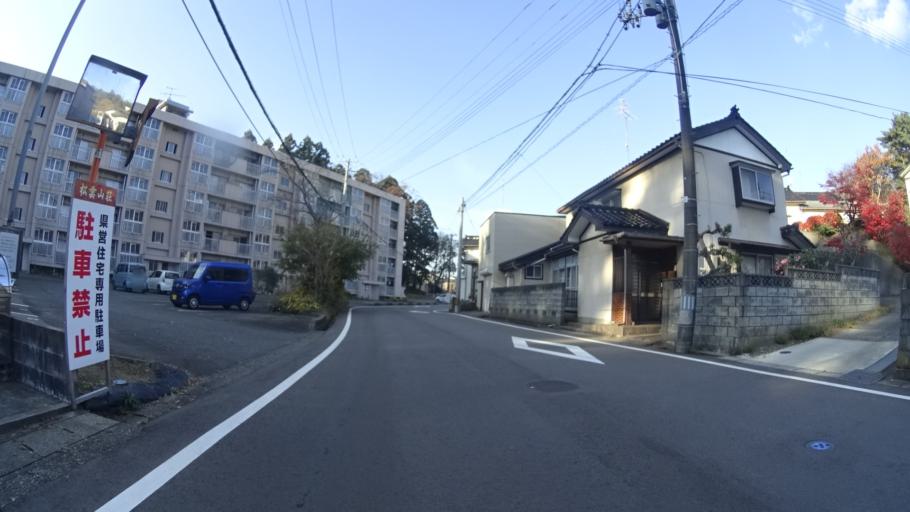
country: JP
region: Niigata
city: Kashiwazaki
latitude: 37.3600
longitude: 138.5456
